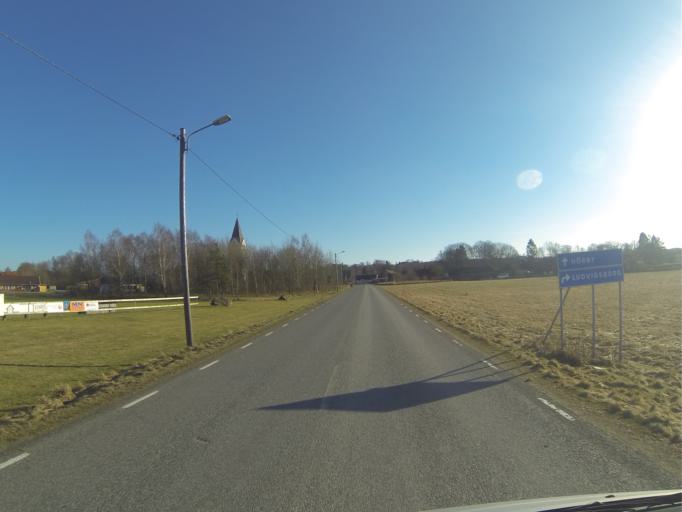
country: SE
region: Skane
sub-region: Horby Kommun
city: Hoerby
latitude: 55.9264
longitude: 13.6682
